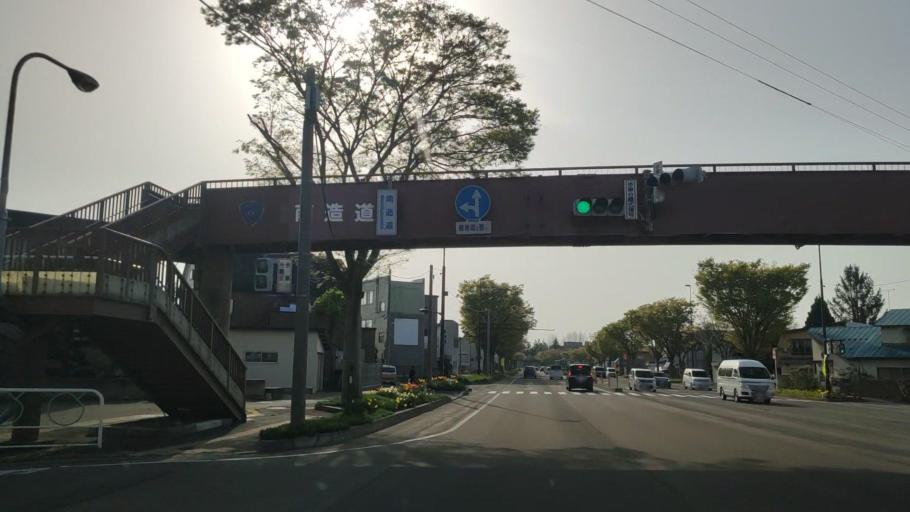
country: JP
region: Aomori
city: Aomori Shi
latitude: 40.8276
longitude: 140.7919
